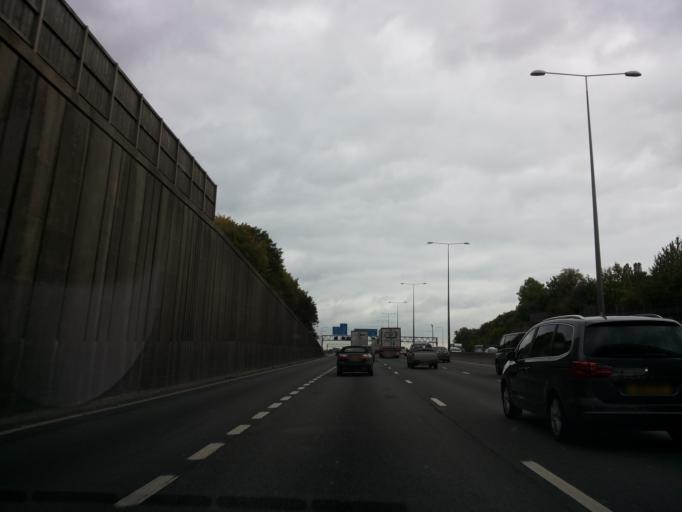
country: GB
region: England
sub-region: Hertfordshire
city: Shenley AV
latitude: 51.6917
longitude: -0.2363
